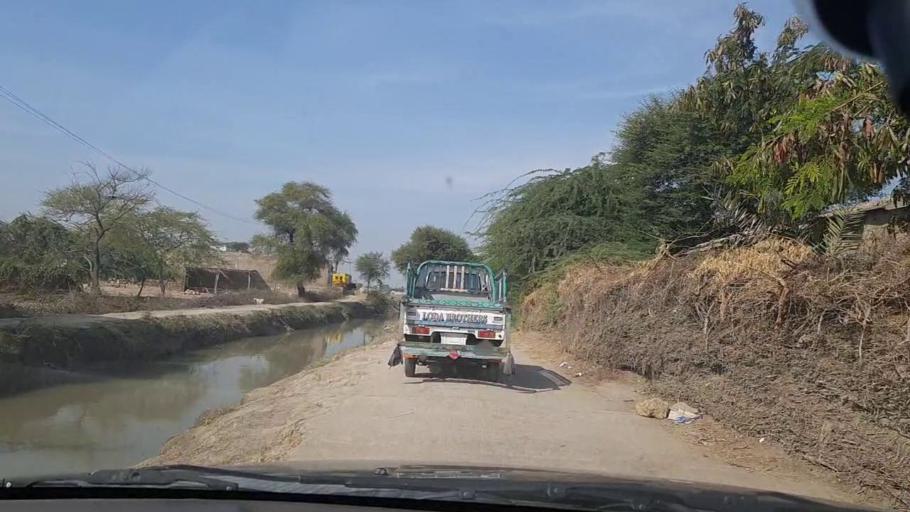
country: PK
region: Sindh
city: Mirpur Batoro
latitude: 24.7351
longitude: 68.2568
